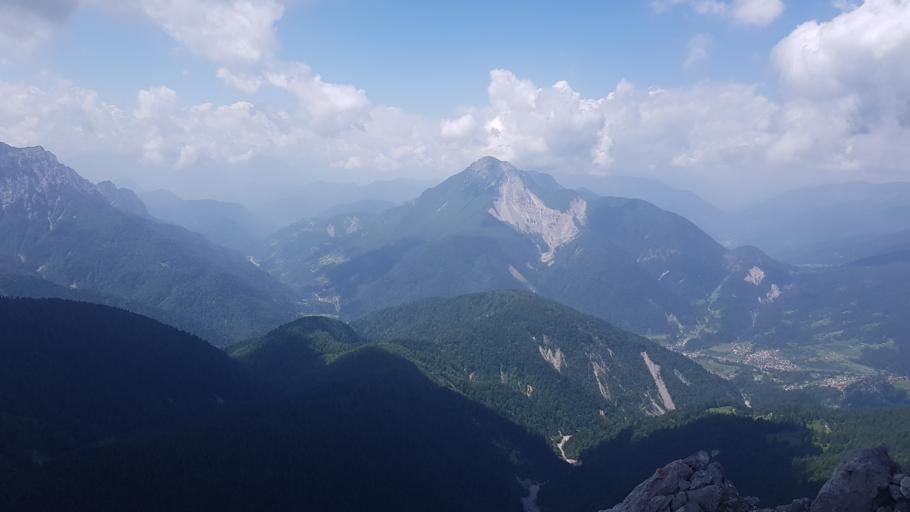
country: IT
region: Friuli Venezia Giulia
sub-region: Provincia di Udine
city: Paularo
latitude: 46.5364
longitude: 13.1801
